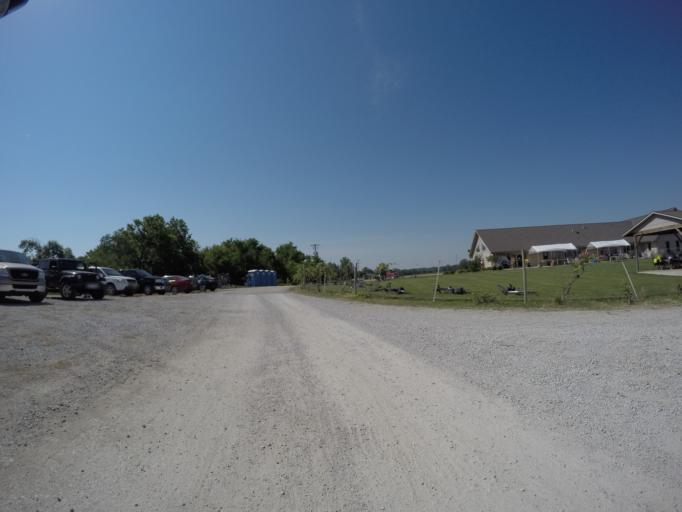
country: US
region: Nebraska
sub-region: Pawnee County
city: Pawnee City
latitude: 40.1151
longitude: -96.1631
